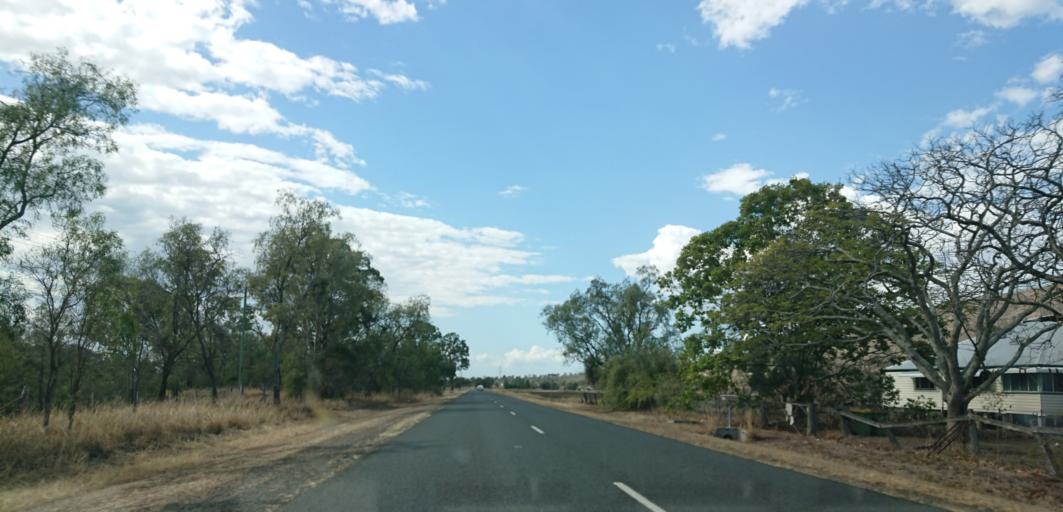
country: AU
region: Queensland
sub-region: Lockyer Valley
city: Gatton
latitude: -27.6509
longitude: 152.1730
